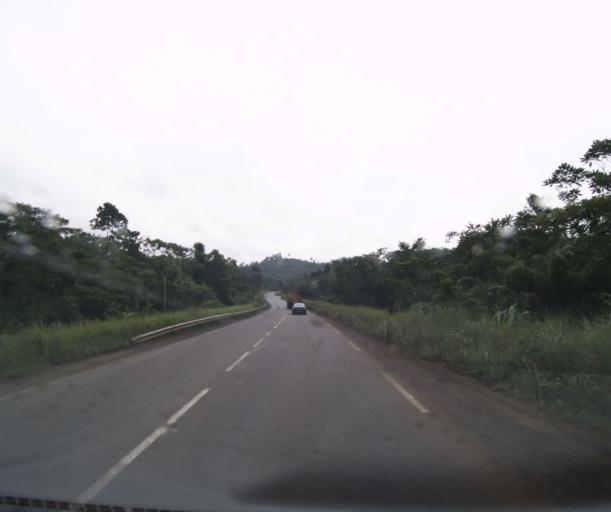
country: CM
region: Littoral
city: Edea
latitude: 3.7806
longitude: 10.2006
